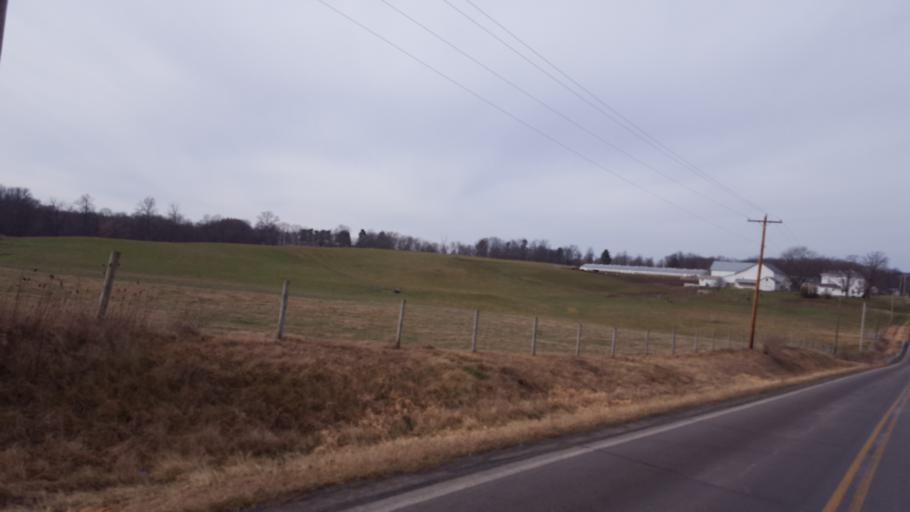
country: US
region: Ohio
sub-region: Wayne County
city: Apple Creek
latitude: 40.6919
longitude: -81.8800
